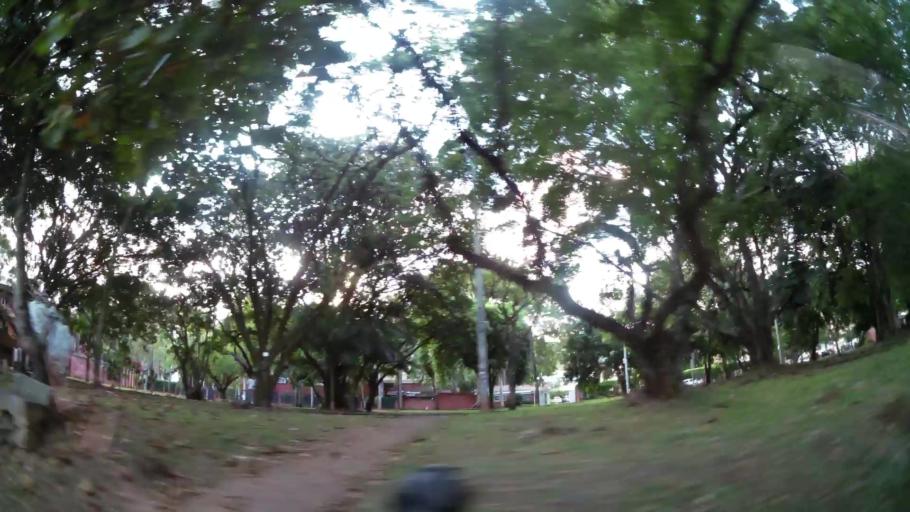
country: CO
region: Valle del Cauca
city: Cali
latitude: 3.4064
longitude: -76.5517
